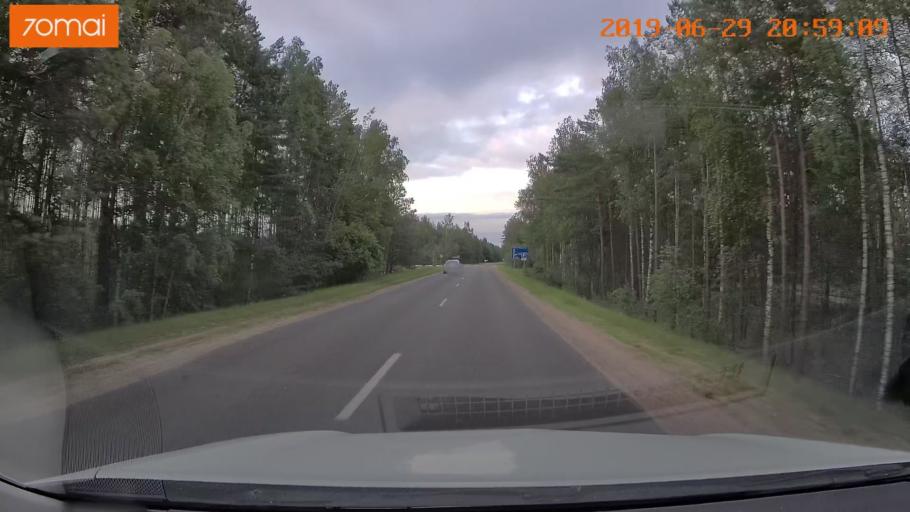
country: BY
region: Brest
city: Hantsavichy
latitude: 52.7355
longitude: 26.4004
